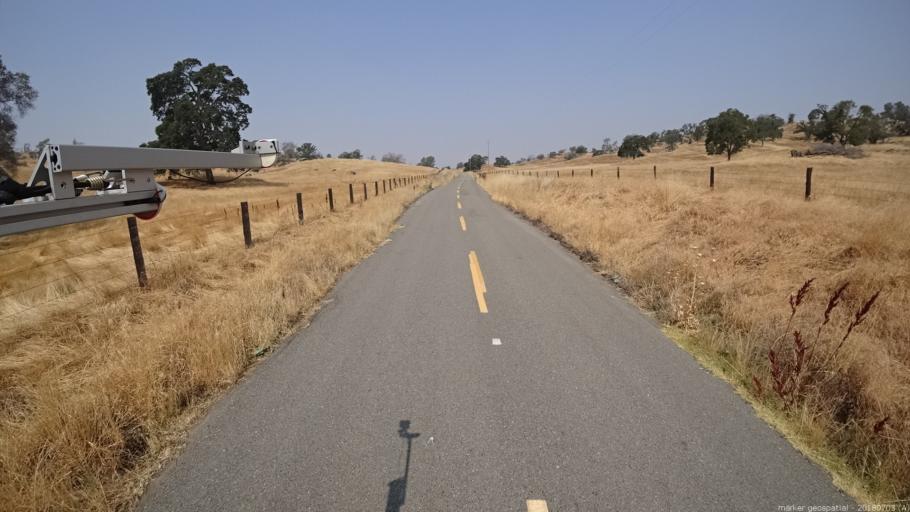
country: US
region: California
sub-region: Madera County
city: Yosemite Lakes
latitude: 37.0575
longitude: -119.7212
